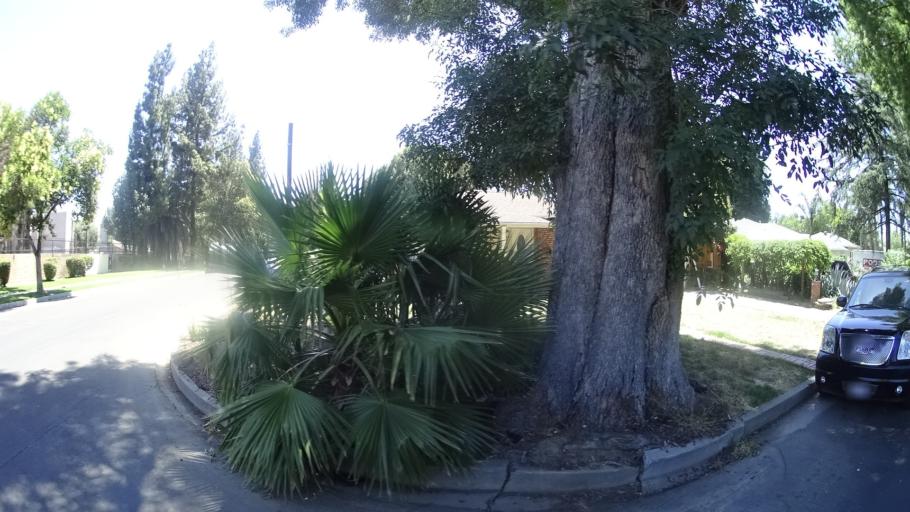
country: US
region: California
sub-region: Los Angeles County
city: Northridge
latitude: 34.1992
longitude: -118.5216
